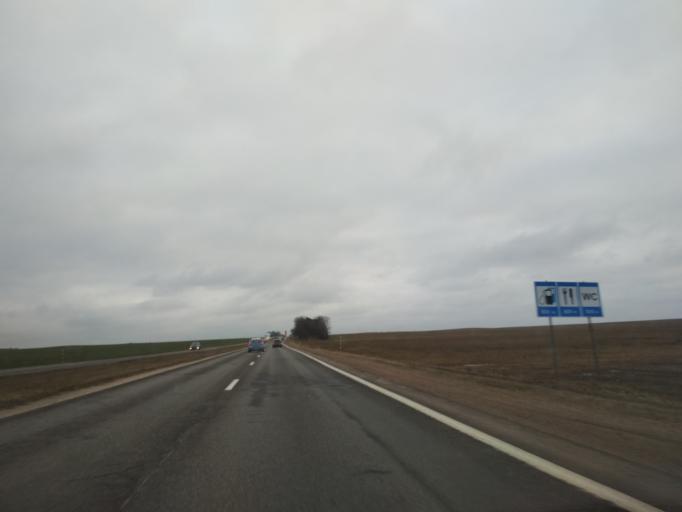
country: BY
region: Minsk
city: Blon'
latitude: 53.5556
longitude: 28.1533
